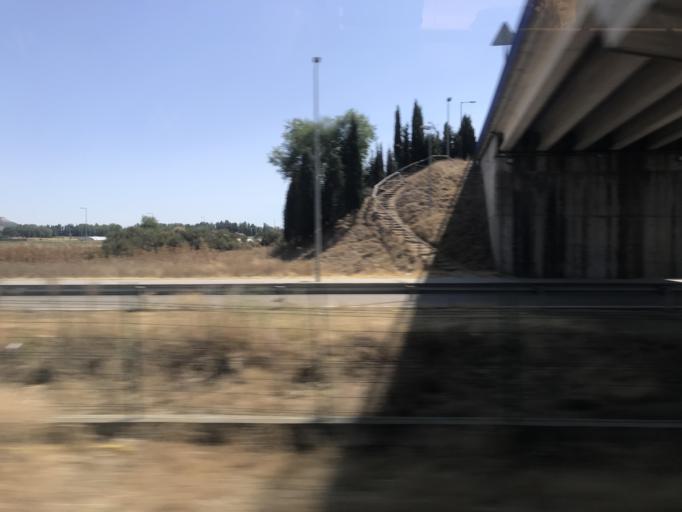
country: ES
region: Castille and Leon
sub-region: Provincia de Valladolid
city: Valladolid
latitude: 41.6646
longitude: -4.7012
